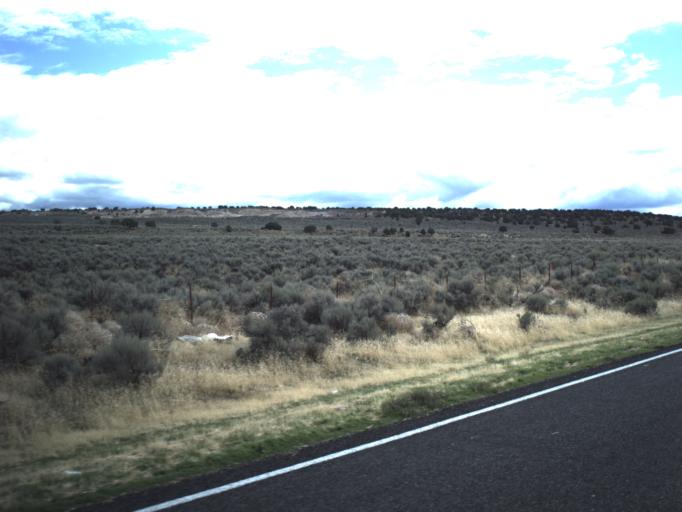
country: US
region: Utah
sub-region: Millard County
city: Fillmore
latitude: 39.0126
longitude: -112.4100
